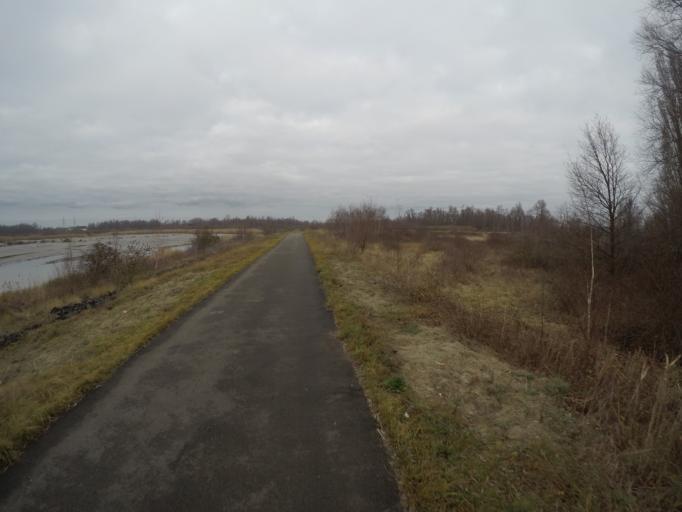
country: BE
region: Flanders
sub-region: Provincie Antwerpen
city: Hoboken
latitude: 51.2072
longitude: 4.3621
